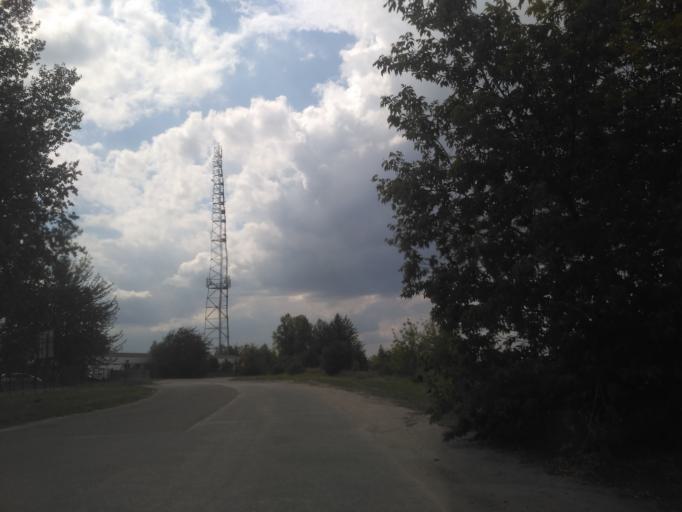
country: PL
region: Lublin Voivodeship
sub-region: Powiat lubelski
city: Jakubowice Murowane
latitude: 51.2363
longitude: 22.6178
